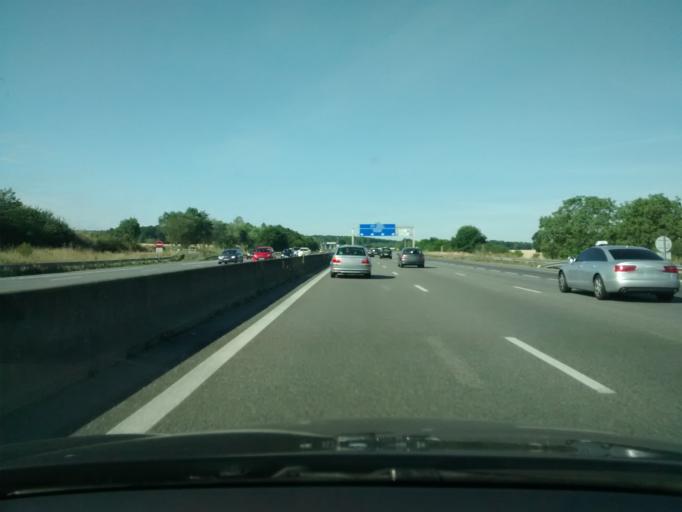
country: FR
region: Ile-de-France
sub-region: Departement de l'Essonne
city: Saint-Cyr-sous-Dourdan
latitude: 48.5730
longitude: 1.9985
